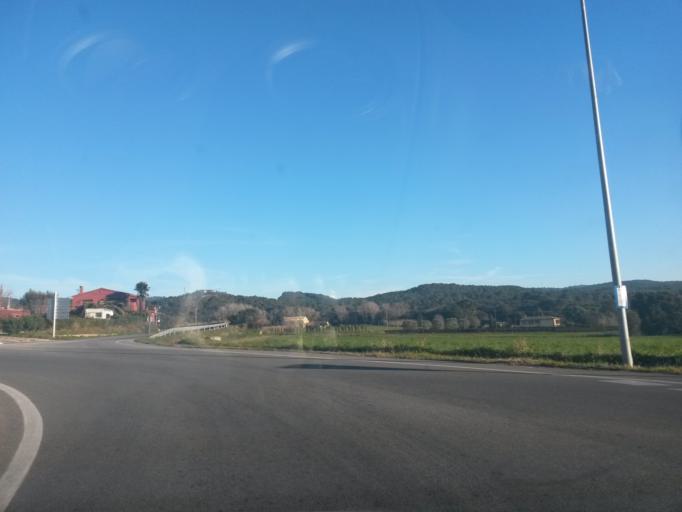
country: ES
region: Catalonia
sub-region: Provincia de Girona
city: Regencos
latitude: 41.9510
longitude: 3.1677
